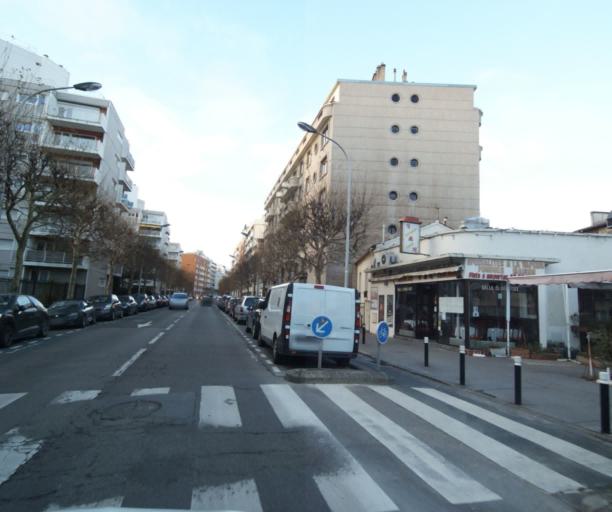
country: FR
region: Ile-de-France
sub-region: Departement des Hauts-de-Seine
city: Courbevoie
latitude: 48.9027
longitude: 2.2660
